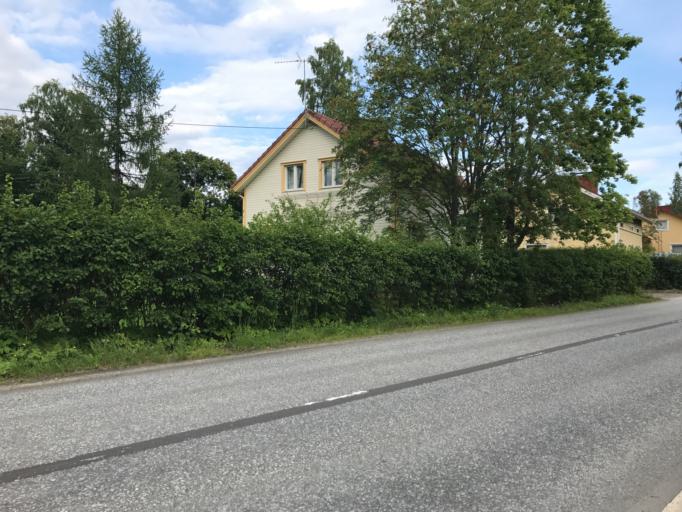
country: FI
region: Pirkanmaa
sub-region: Etelae-Pirkanmaa
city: Valkeakoski
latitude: 61.2515
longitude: 24.0495
